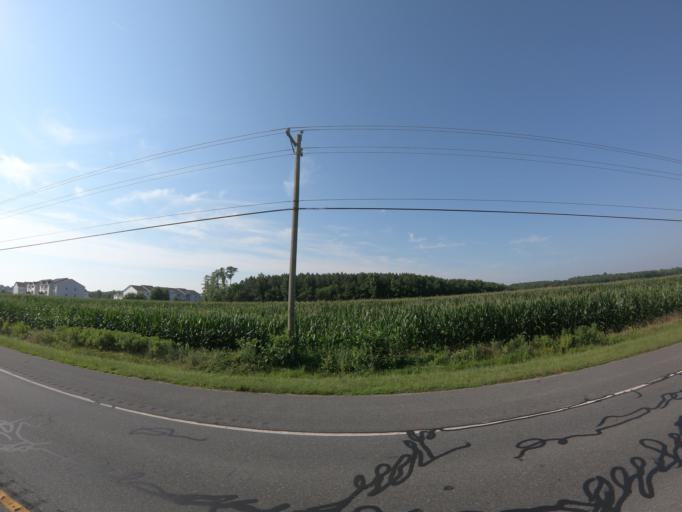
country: US
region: Delaware
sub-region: Sussex County
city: Georgetown
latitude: 38.6988
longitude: -75.4175
